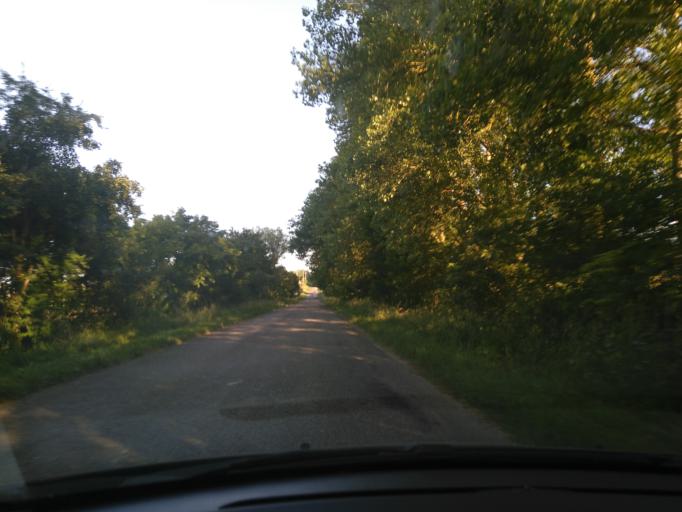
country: FR
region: Midi-Pyrenees
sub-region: Departement du Gers
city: Valence-sur-Baise
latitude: 43.8895
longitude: 0.3708
